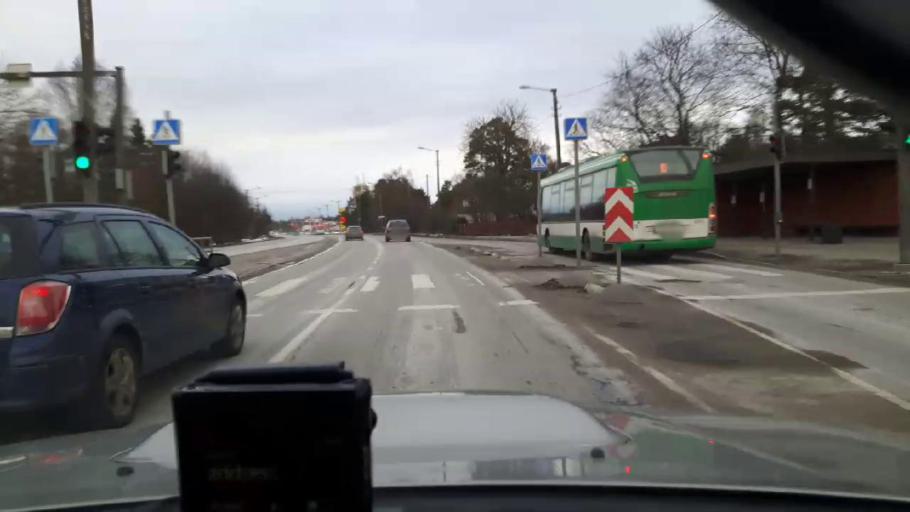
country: EE
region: Harju
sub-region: Saue vald
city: Laagri
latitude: 59.3560
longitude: 24.6310
